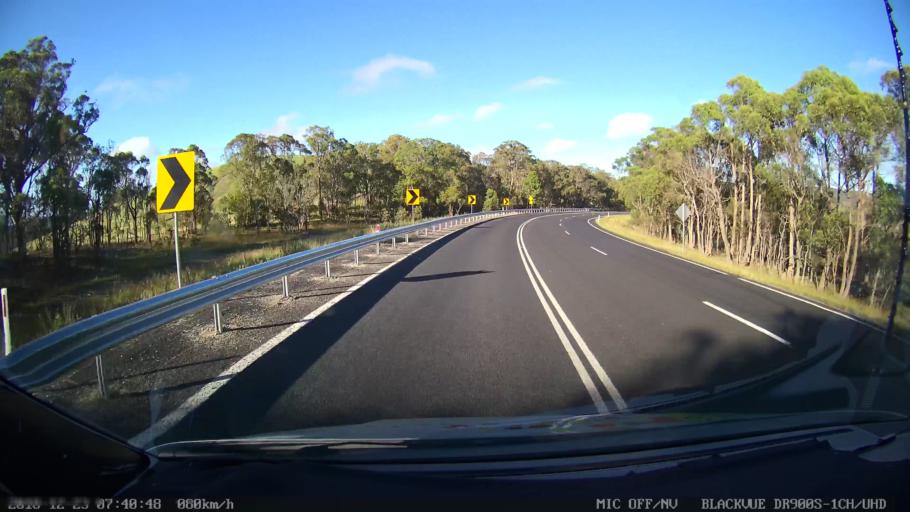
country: AU
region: New South Wales
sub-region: Armidale Dumaresq
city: Enmore
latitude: -30.5156
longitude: 152.0020
